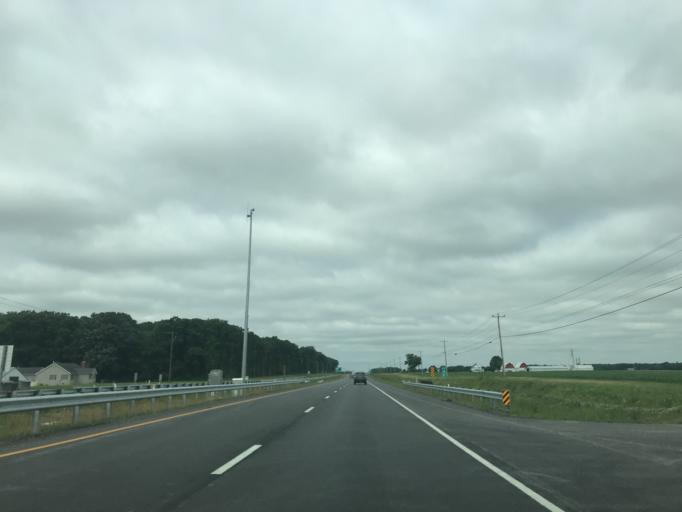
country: US
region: Maryland
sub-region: Caroline County
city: Ridgely
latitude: 38.9277
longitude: -75.9986
